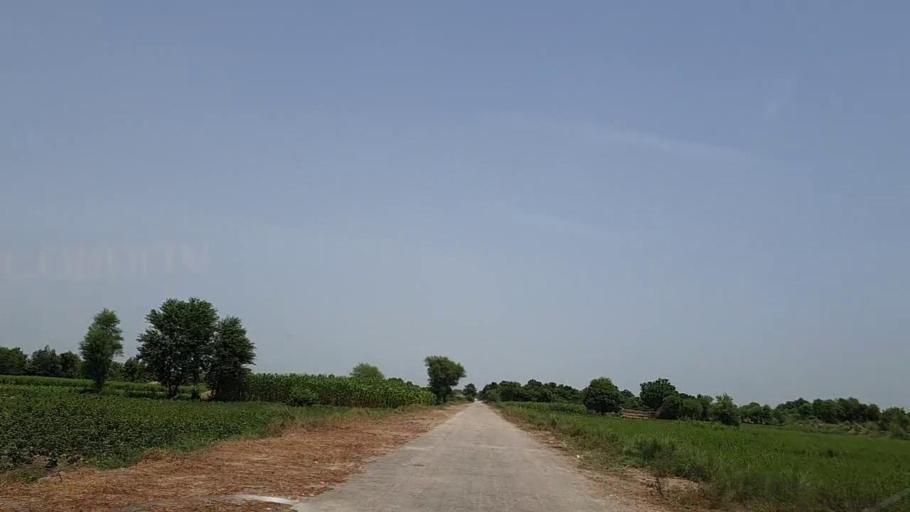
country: PK
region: Sindh
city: Tharu Shah
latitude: 26.9453
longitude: 68.0252
